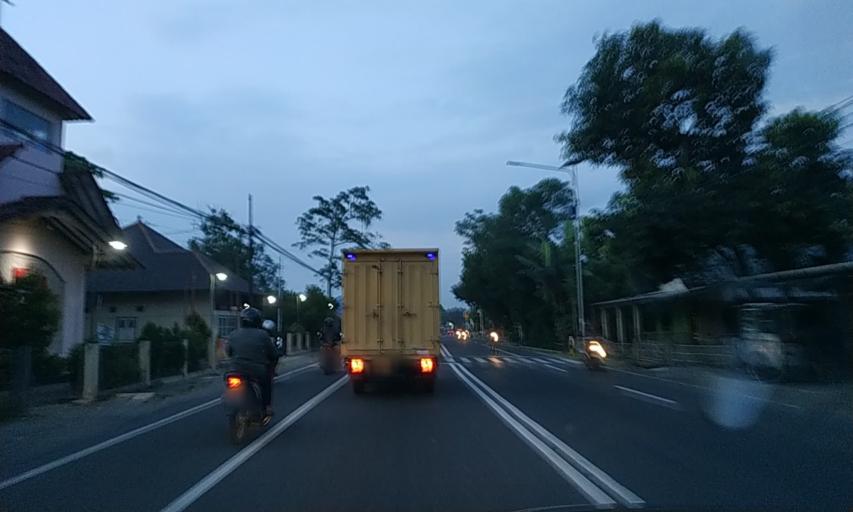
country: ID
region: Daerah Istimewa Yogyakarta
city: Srandakan
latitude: -7.8433
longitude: 110.2184
